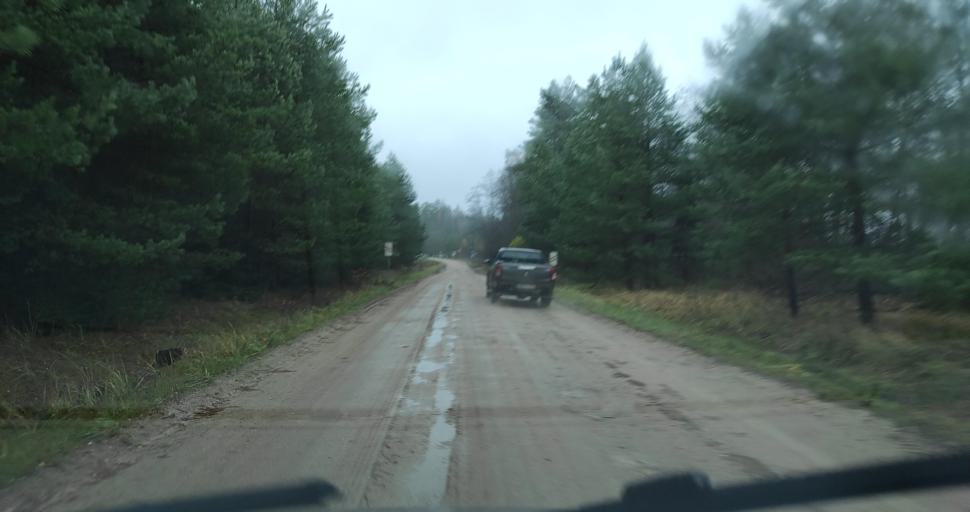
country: LV
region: Skrunda
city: Skrunda
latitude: 56.6887
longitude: 22.0781
